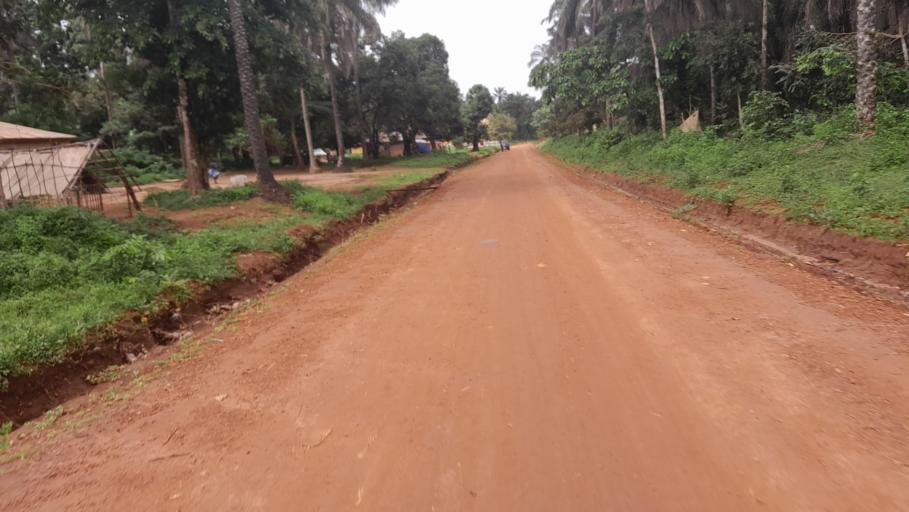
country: GN
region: Boke
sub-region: Boffa
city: Boffa
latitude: 10.0031
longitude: -13.8858
